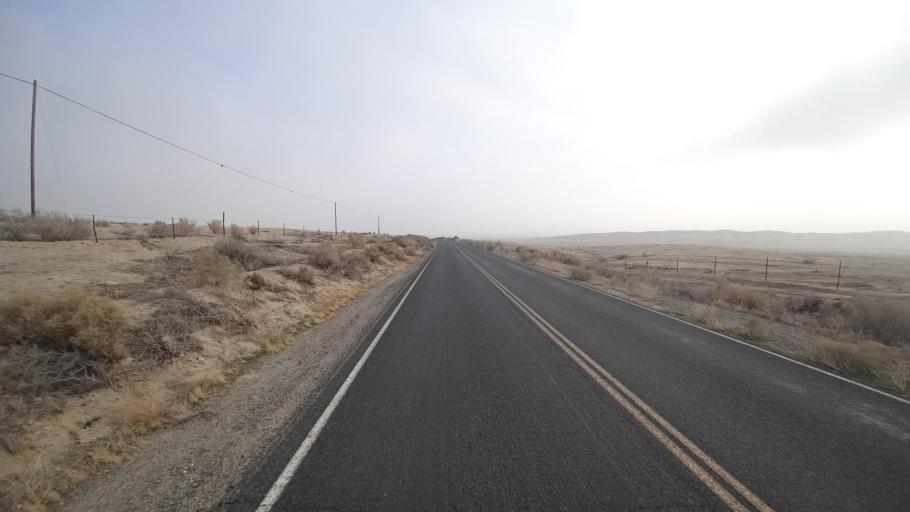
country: US
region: California
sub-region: Kern County
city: Ford City
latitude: 35.2492
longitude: -119.4624
